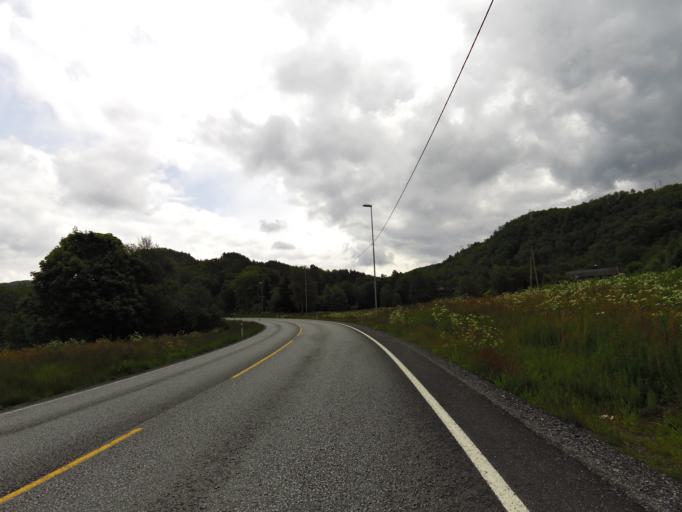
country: NO
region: Vest-Agder
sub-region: Lyngdal
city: Lyngdal
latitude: 58.1122
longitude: 6.9520
